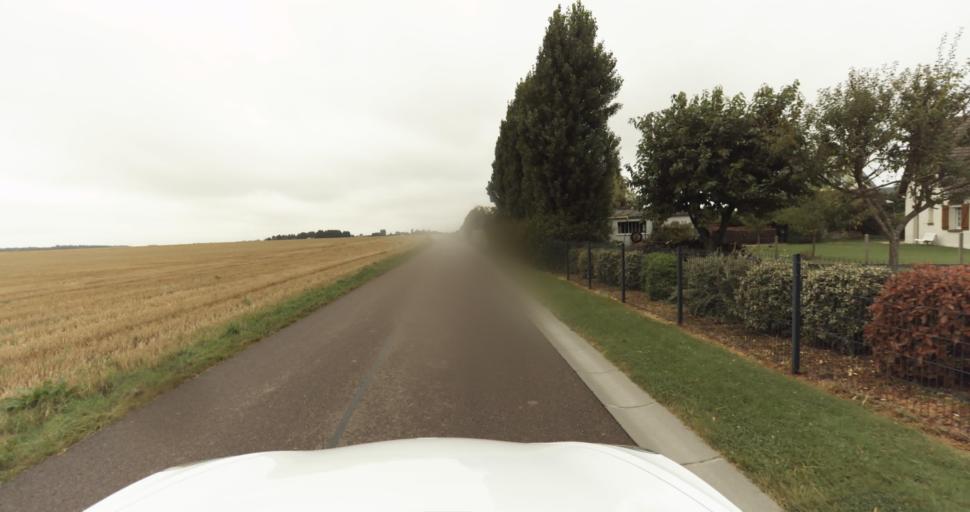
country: FR
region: Haute-Normandie
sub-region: Departement de l'Eure
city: Aviron
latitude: 49.0684
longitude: 1.1140
